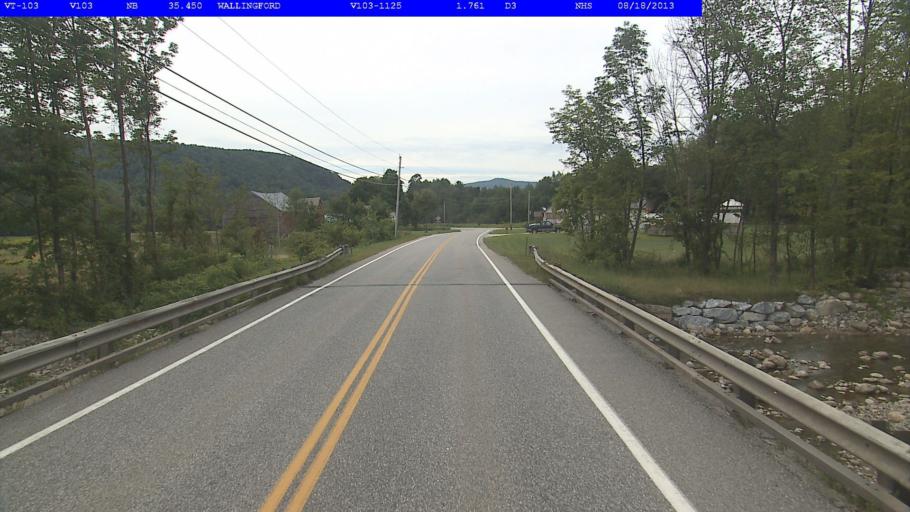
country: US
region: Vermont
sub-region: Rutland County
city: Rutland
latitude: 43.4705
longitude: -72.8858
